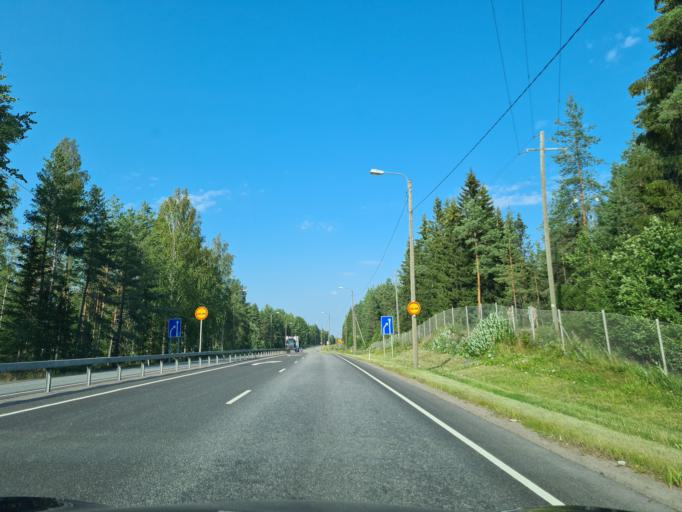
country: FI
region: Satakunta
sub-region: Pohjois-Satakunta
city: Kankaanpaeae
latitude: 61.8207
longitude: 22.3757
